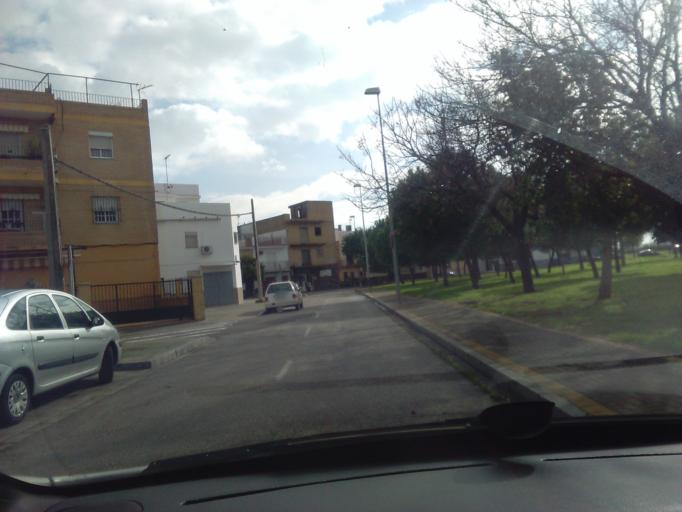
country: ES
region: Andalusia
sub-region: Provincia de Sevilla
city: Sevilla
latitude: 37.3827
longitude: -5.9134
